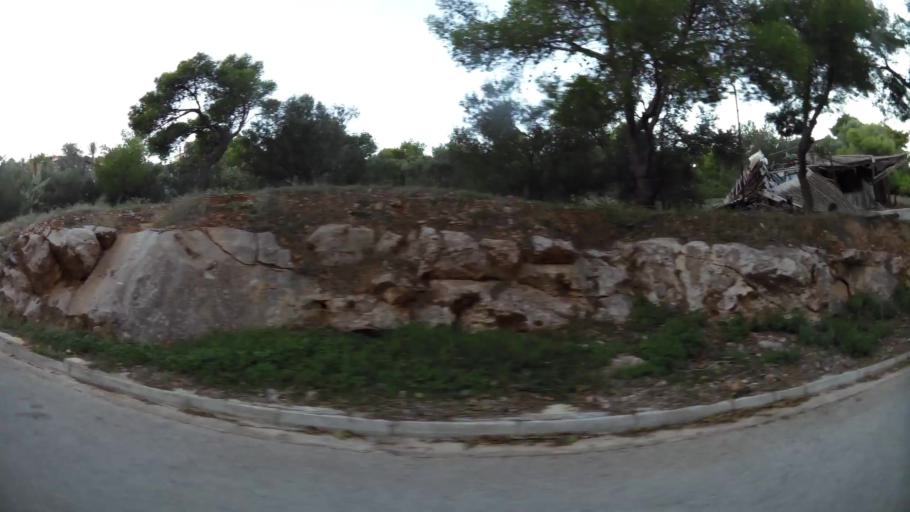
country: GR
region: Attica
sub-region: Nomarchia Anatolikis Attikis
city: Vouliagmeni
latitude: 37.8170
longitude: 23.7932
